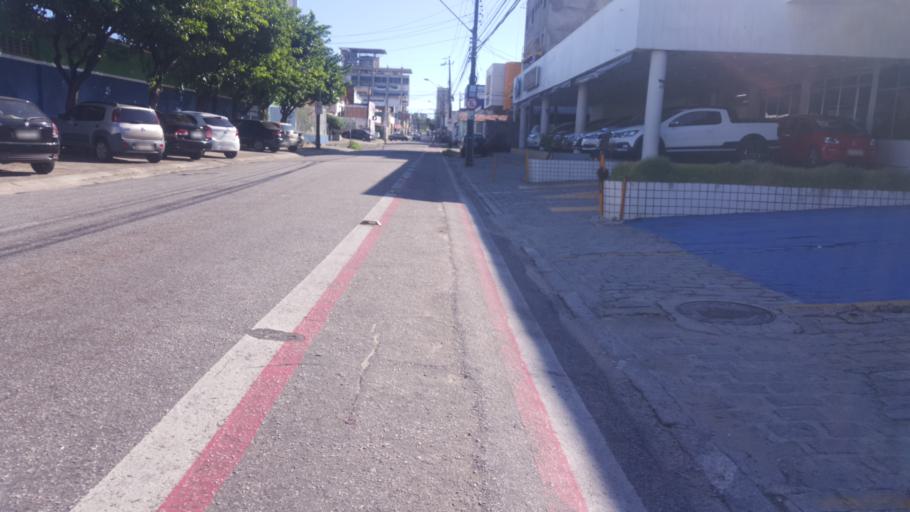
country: BR
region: Ceara
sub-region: Fortaleza
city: Fortaleza
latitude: -3.7393
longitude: -38.5323
